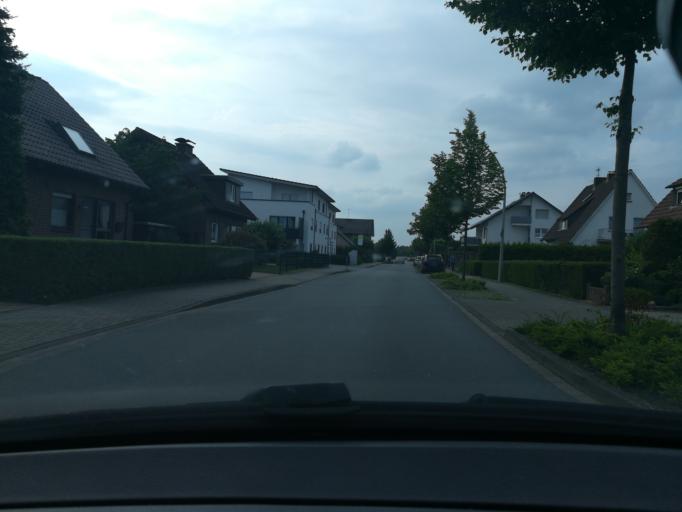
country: DE
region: North Rhine-Westphalia
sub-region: Regierungsbezirk Detmold
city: Oerlinghausen
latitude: 51.9126
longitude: 8.6050
